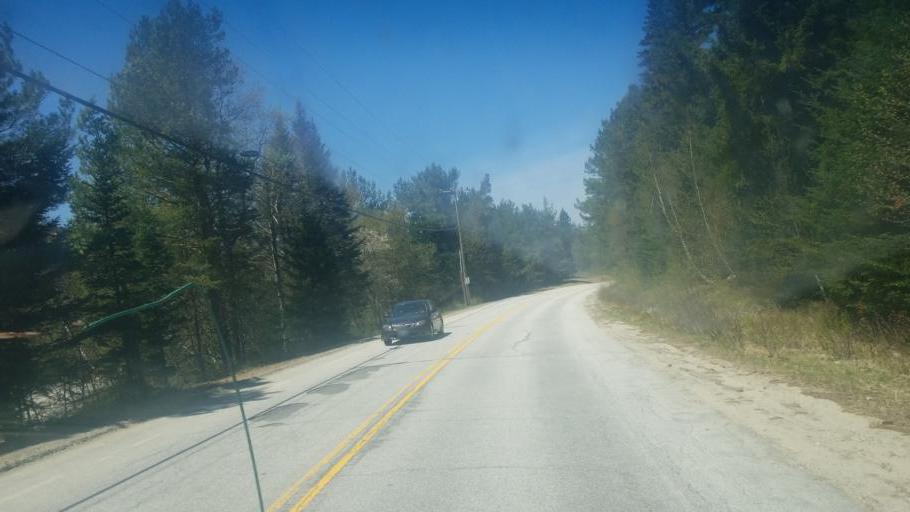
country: US
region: New Hampshire
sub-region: Coos County
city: Jefferson
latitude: 44.2597
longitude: -71.4499
